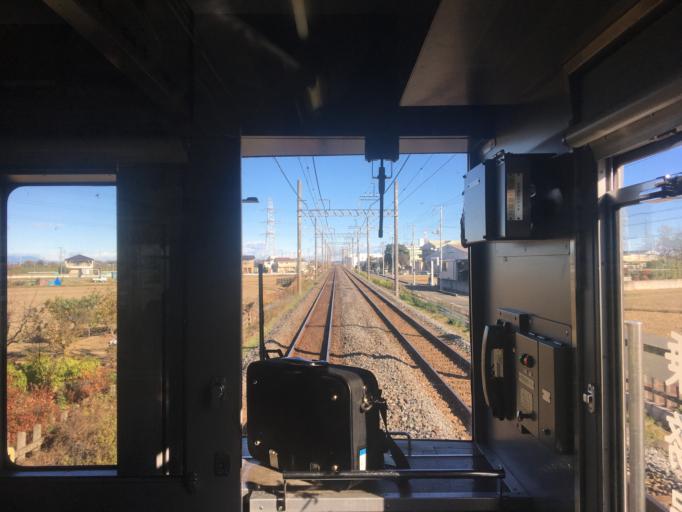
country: JP
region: Saitama
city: Sakado
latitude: 35.9782
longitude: 139.3994
